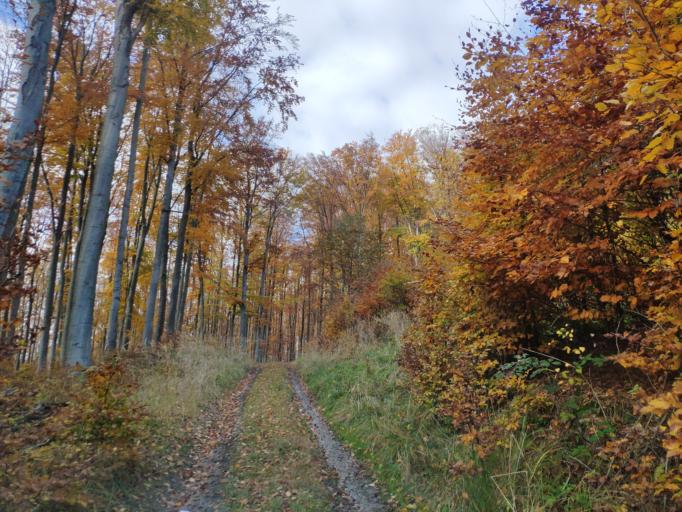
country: SK
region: Kosicky
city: Medzev
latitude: 48.7326
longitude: 20.9974
